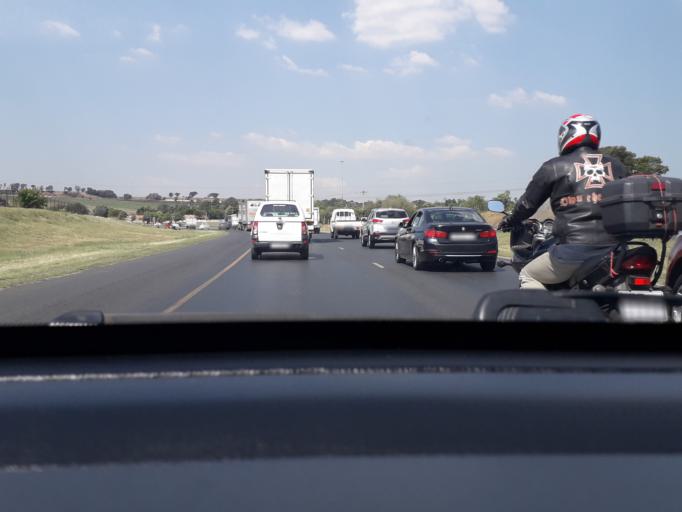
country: ZA
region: Gauteng
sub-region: City of Johannesburg Metropolitan Municipality
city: Modderfontein
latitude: -26.1018
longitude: 28.1807
